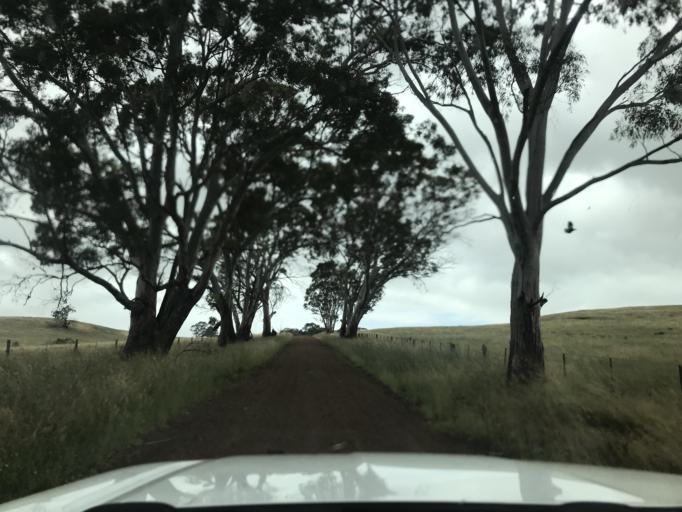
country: AU
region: South Australia
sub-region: Wattle Range
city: Penola
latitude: -37.2346
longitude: 141.4610
